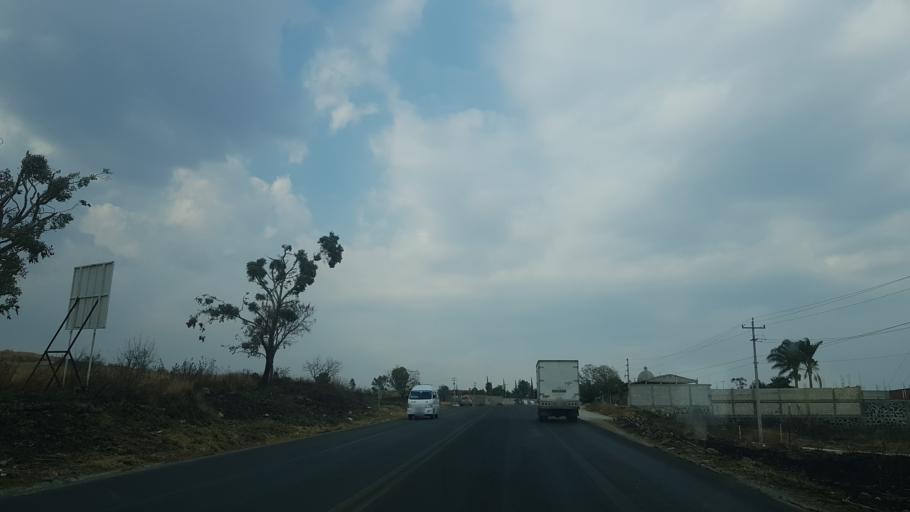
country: MX
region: Puebla
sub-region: Santa Isabel Cholula
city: Santa Ana Acozautla
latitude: 18.9669
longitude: -98.3835
